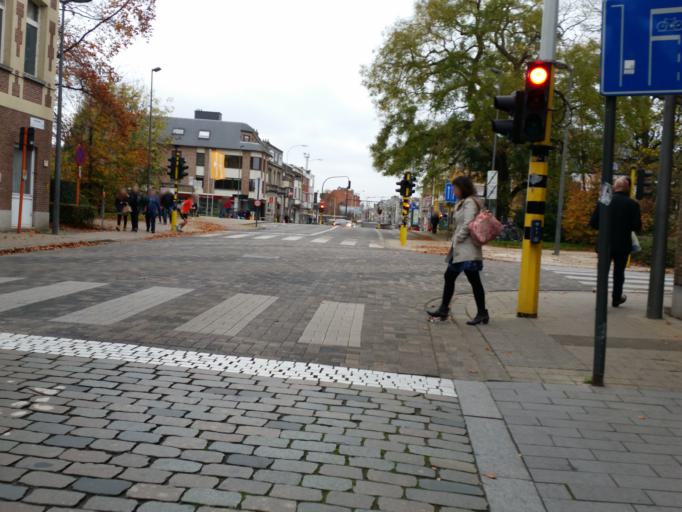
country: BE
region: Flanders
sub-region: Provincie Antwerpen
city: Lier
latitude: 51.1349
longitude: 4.5653
